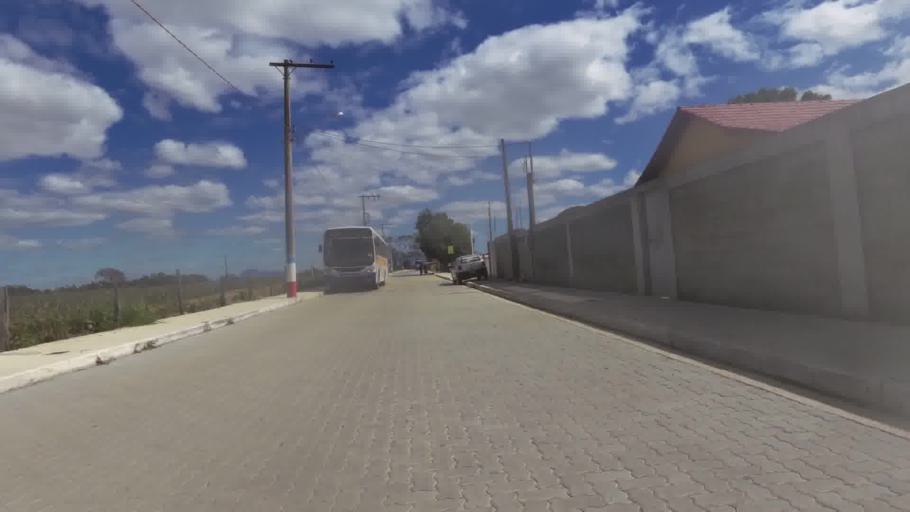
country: BR
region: Espirito Santo
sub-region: Marataizes
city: Marataizes
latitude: -21.1797
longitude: -40.9885
